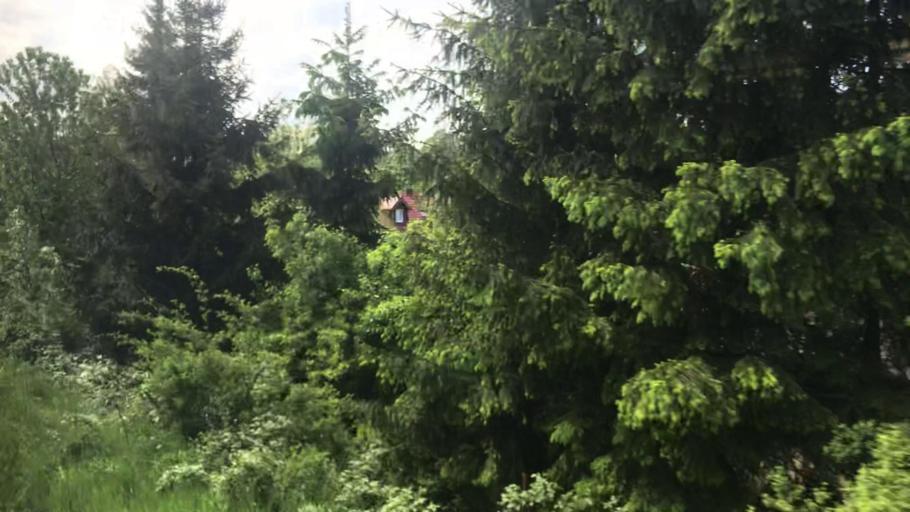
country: PL
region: Lower Silesian Voivodeship
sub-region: Powiat swidnicki
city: Swiebodzice
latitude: 50.8319
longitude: 16.3370
